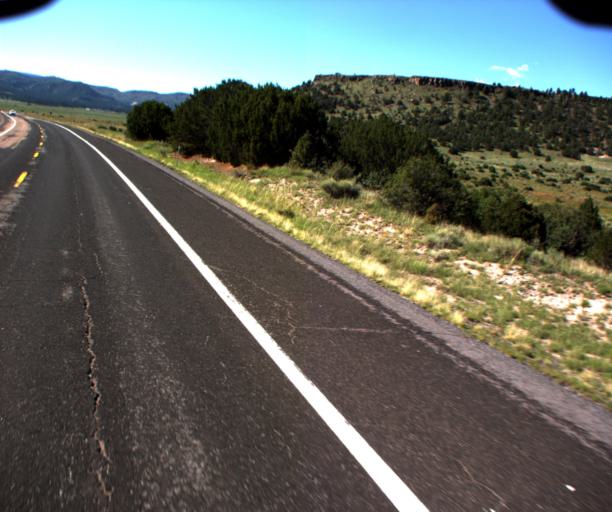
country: US
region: Arizona
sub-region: Apache County
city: Eagar
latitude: 34.0335
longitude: -109.1857
